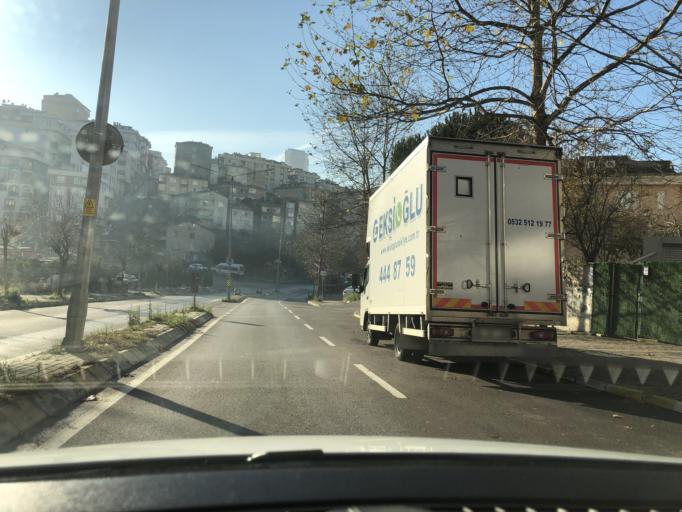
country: TR
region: Istanbul
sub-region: Atasehir
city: Atasehir
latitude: 40.9735
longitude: 29.1254
